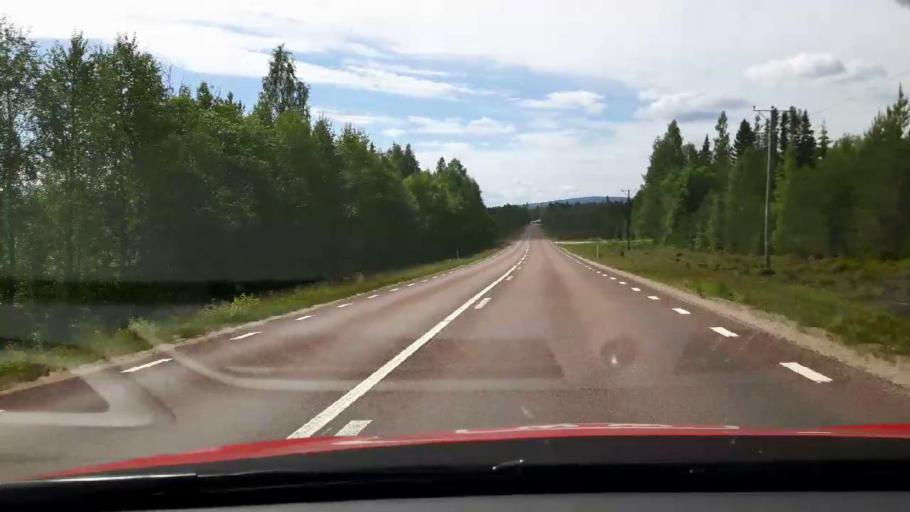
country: SE
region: Jaemtland
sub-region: Harjedalens Kommun
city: Sveg
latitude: 62.0599
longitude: 14.9113
